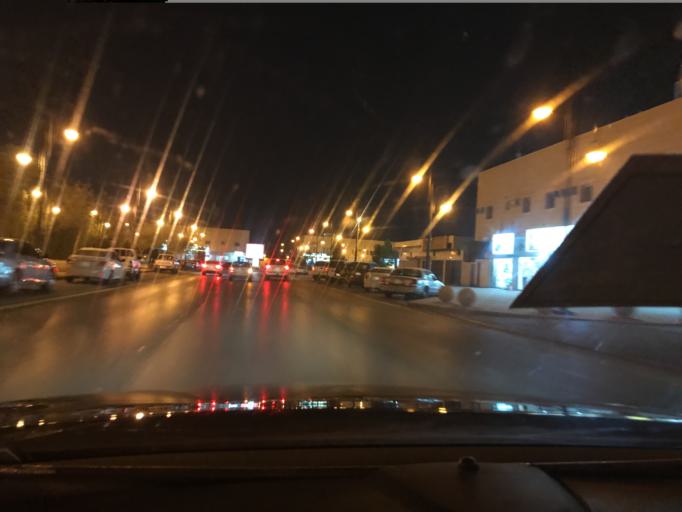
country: SA
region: Ar Riyad
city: Riyadh
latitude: 24.7415
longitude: 46.7668
